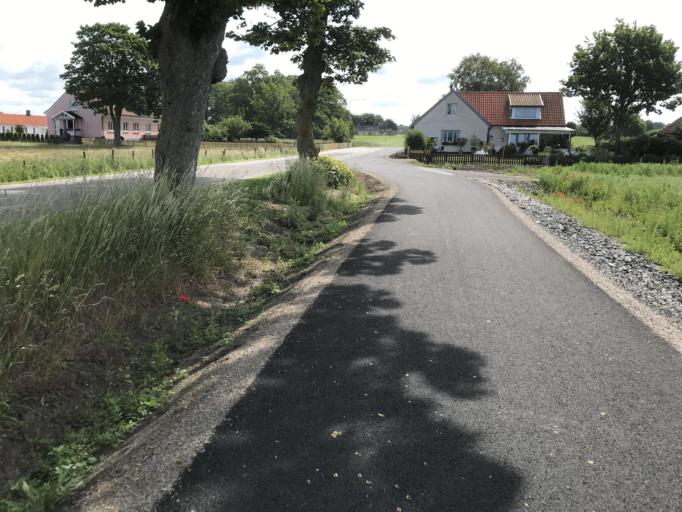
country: SE
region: Skane
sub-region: Helsingborg
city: Rydeback
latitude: 55.9441
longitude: 12.7791
